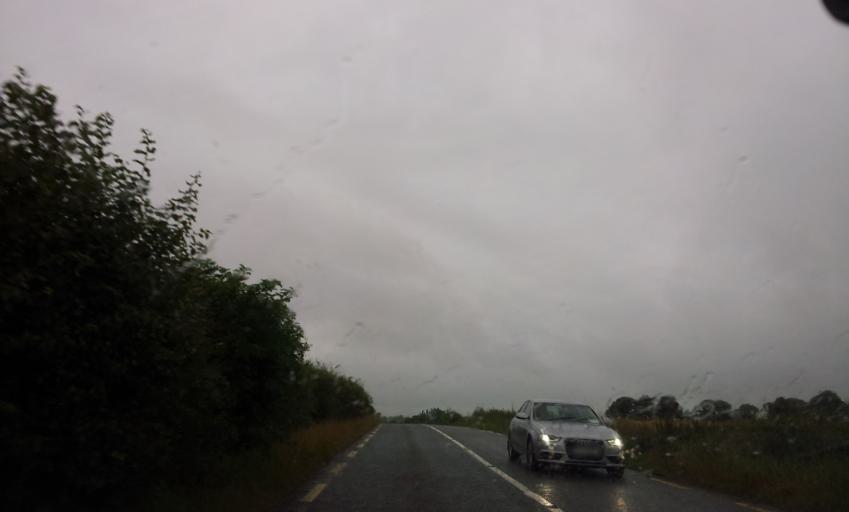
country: IE
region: Munster
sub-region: County Cork
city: Mallow
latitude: 52.1646
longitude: -8.5841
